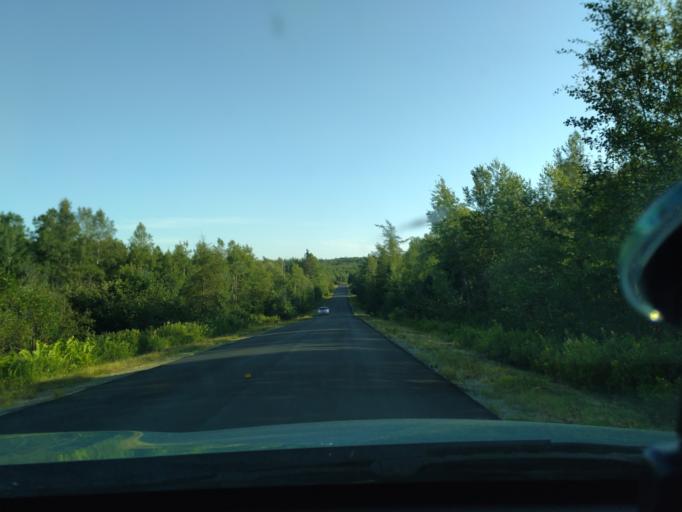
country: US
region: Maine
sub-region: Washington County
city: Eastport
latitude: 44.7234
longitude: -67.1329
